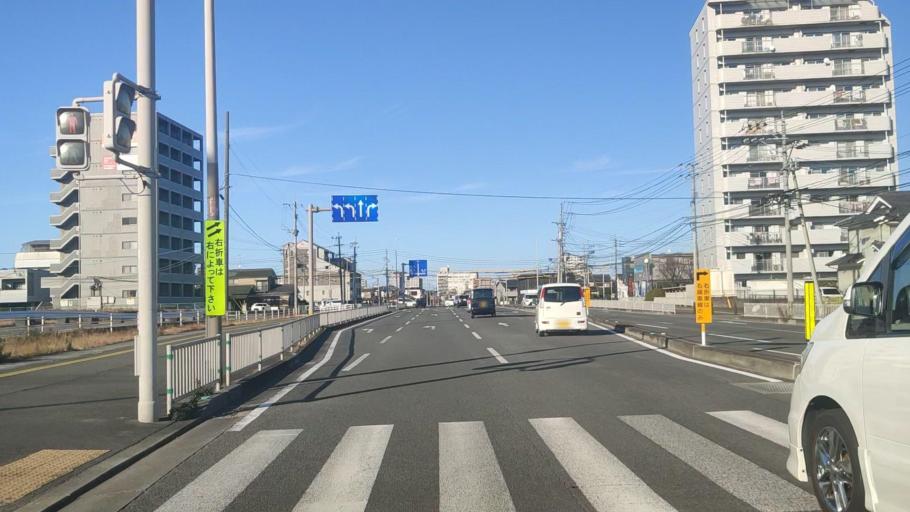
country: JP
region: Oita
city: Oita
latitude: 33.2302
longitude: 131.6189
